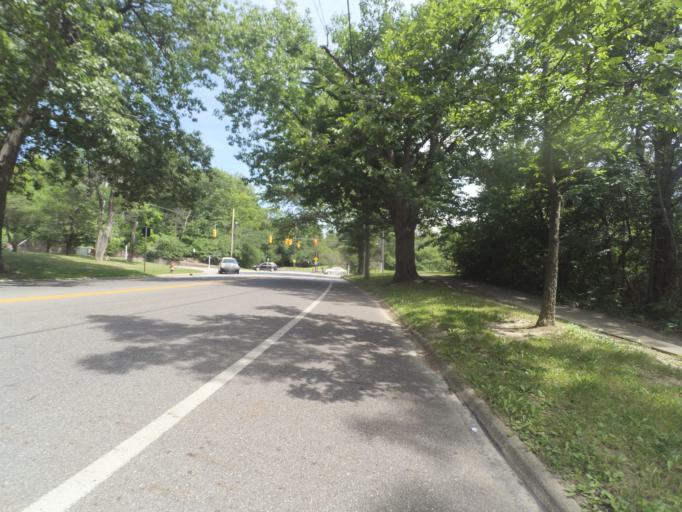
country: US
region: Ohio
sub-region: Cuyahoga County
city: Shaker Heights
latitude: 41.4847
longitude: -81.5658
